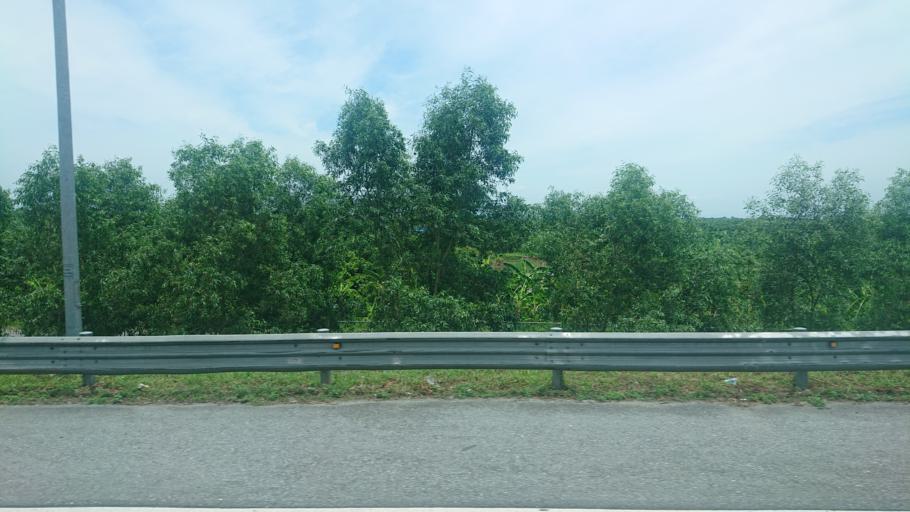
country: VN
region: Hai Phong
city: An Lao
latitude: 20.8098
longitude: 106.5077
